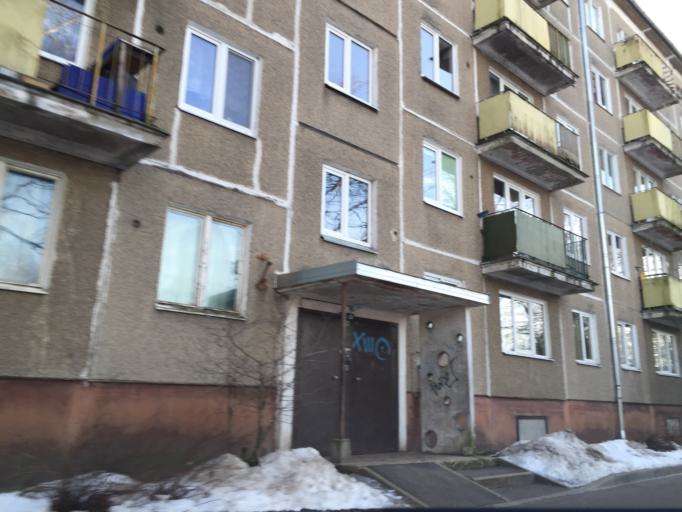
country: LV
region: Riga
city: Bergi
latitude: 56.9842
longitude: 24.2460
